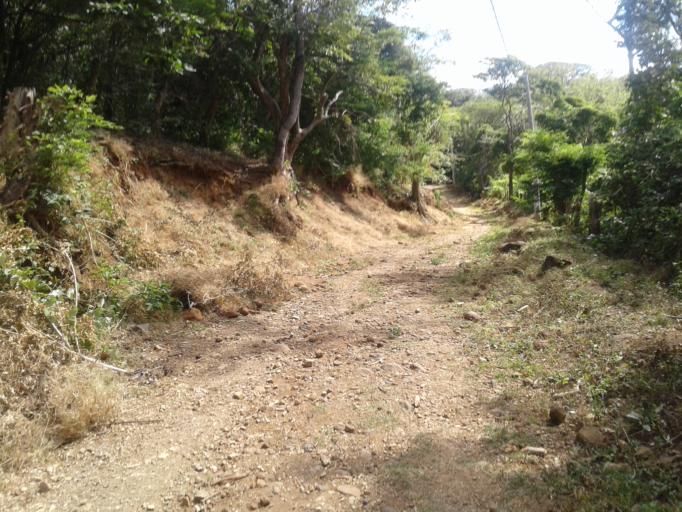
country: NI
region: Carazo
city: Santa Teresa
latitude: 11.6132
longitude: -86.1803
